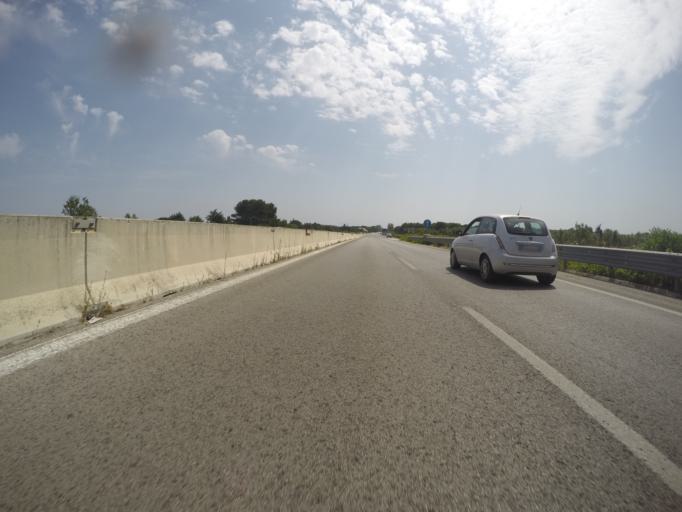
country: IT
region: Apulia
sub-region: Provincia di Brindisi
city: Mesagne
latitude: 40.5677
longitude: 17.7858
